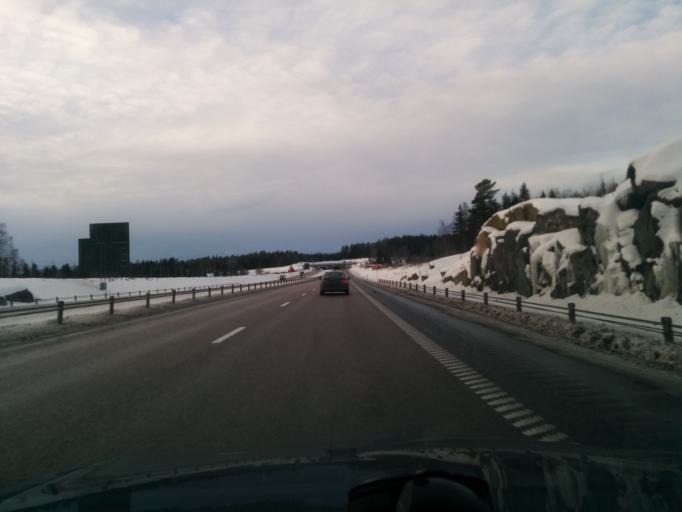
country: SE
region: Uppsala
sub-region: Enkopings Kommun
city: Enkoping
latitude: 59.6441
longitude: 17.0386
